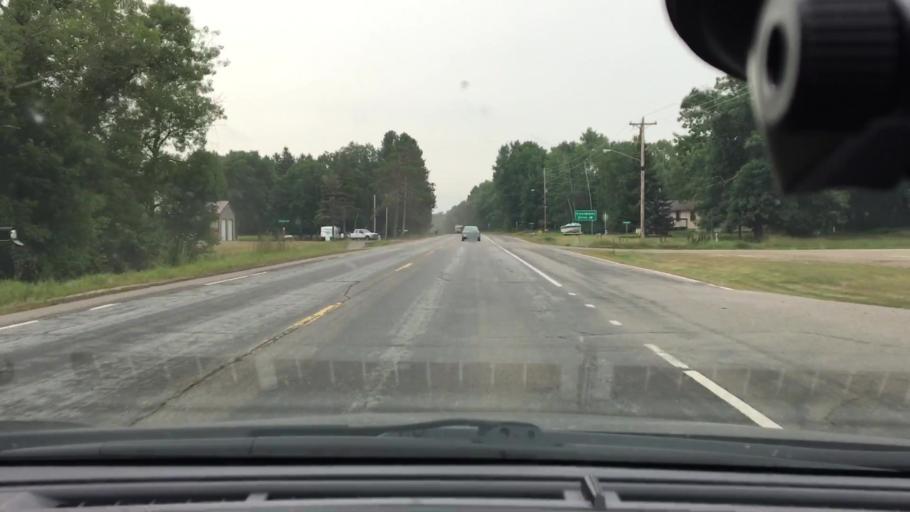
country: US
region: Minnesota
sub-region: Crow Wing County
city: Cross Lake
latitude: 46.7892
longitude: -93.9661
